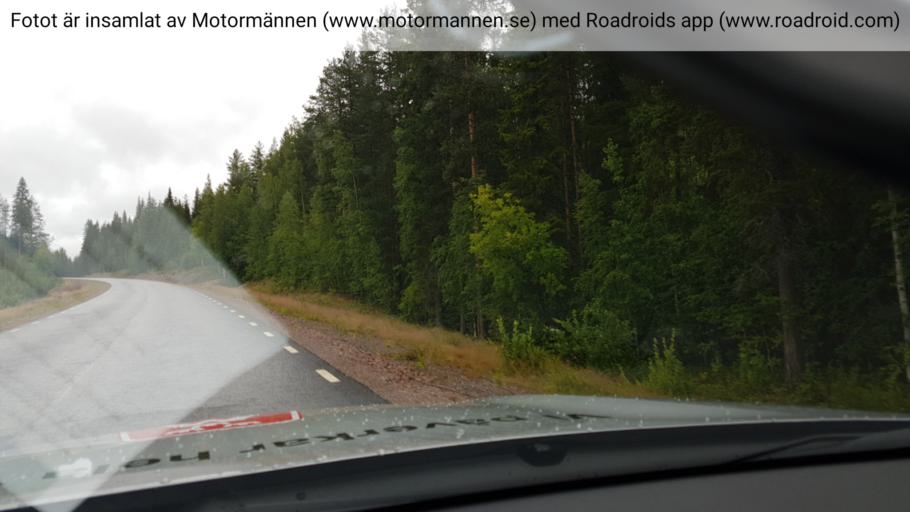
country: SE
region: Norrbotten
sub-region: Gallivare Kommun
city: Gaellivare
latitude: 66.6437
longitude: 20.3939
